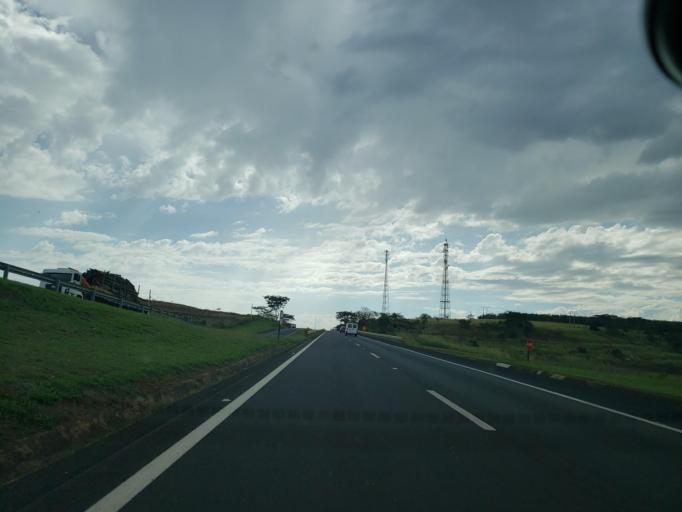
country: BR
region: Sao Paulo
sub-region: Cafelandia
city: Cafelandia
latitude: -21.7623
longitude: -49.6733
